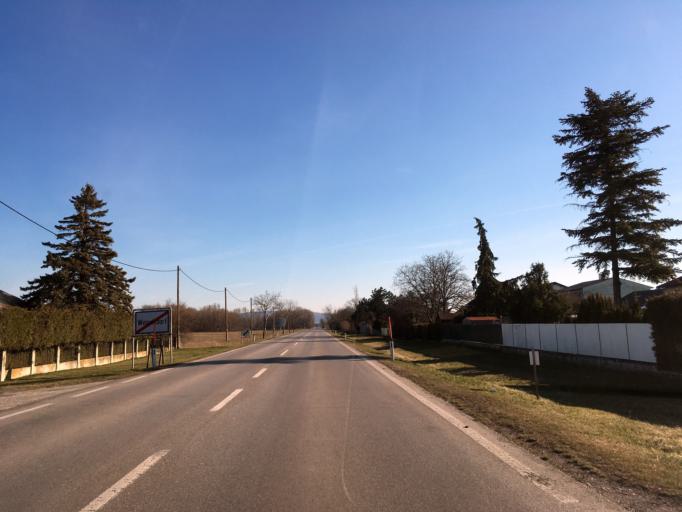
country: AT
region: Lower Austria
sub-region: Politischer Bezirk Baden
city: Ebreichsdorf
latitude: 47.9458
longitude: 16.4106
